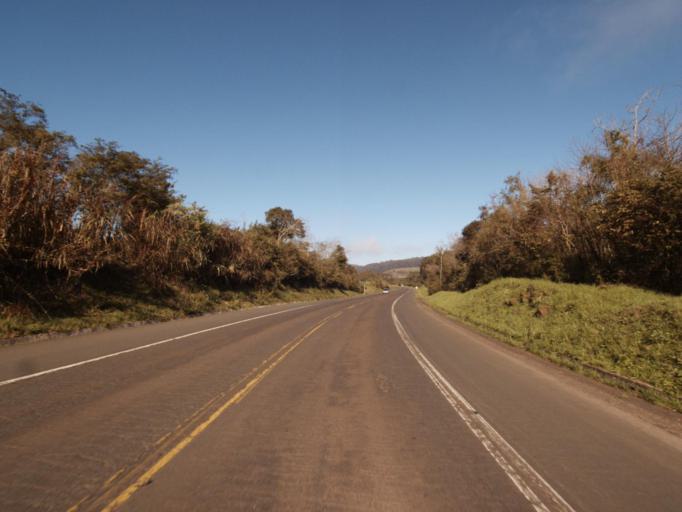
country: BR
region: Rio Grande do Sul
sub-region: Frederico Westphalen
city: Frederico Westphalen
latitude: -26.9921
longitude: -53.2261
